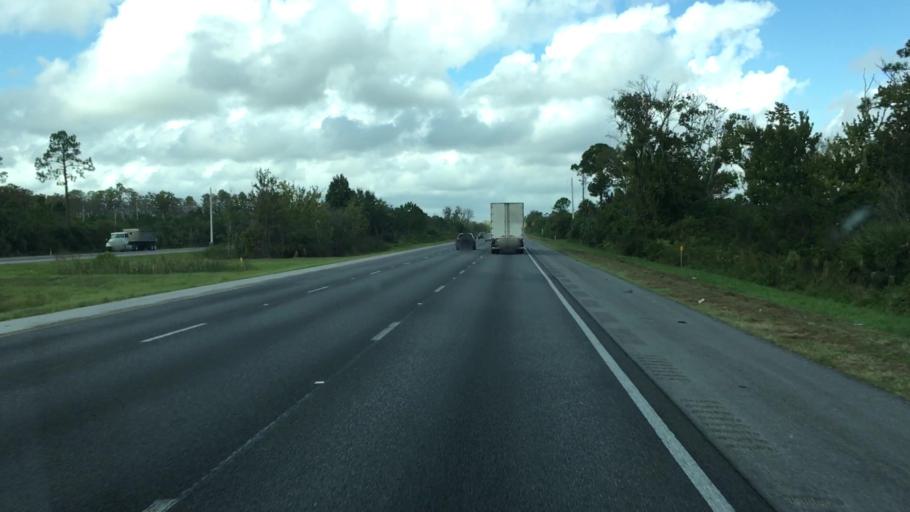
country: US
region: Florida
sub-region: Volusia County
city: Glencoe
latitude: 29.0271
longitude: -80.9969
